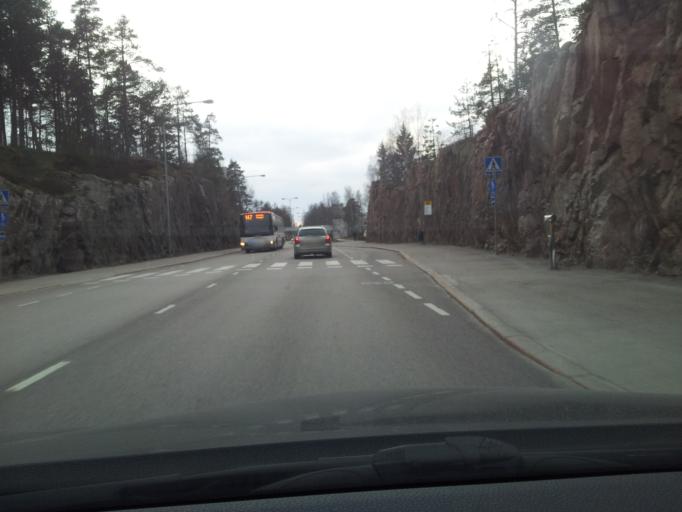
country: FI
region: Uusimaa
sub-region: Helsinki
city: Espoo
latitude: 60.1435
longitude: 24.6736
